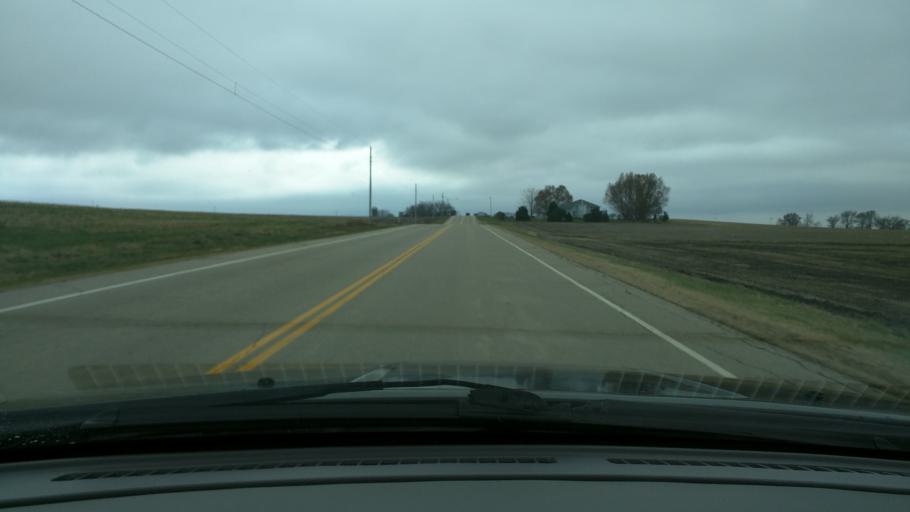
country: US
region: Minnesota
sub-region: Washington County
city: Cottage Grove
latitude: 44.7614
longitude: -92.9239
